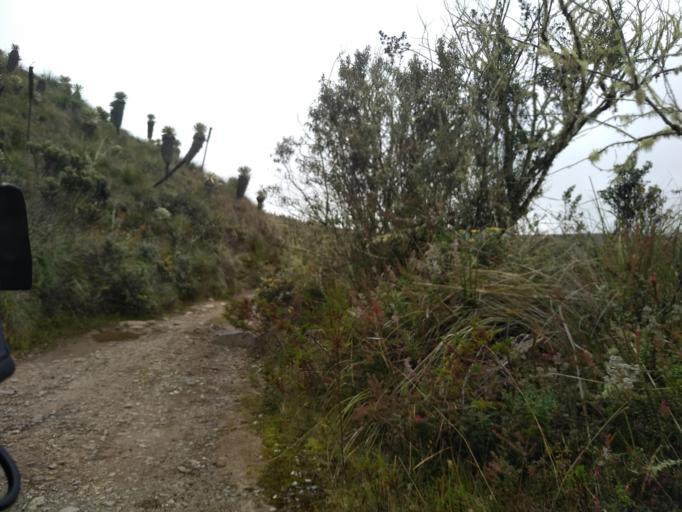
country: EC
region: Carchi
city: San Gabriel
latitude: 0.6931
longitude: -77.8492
